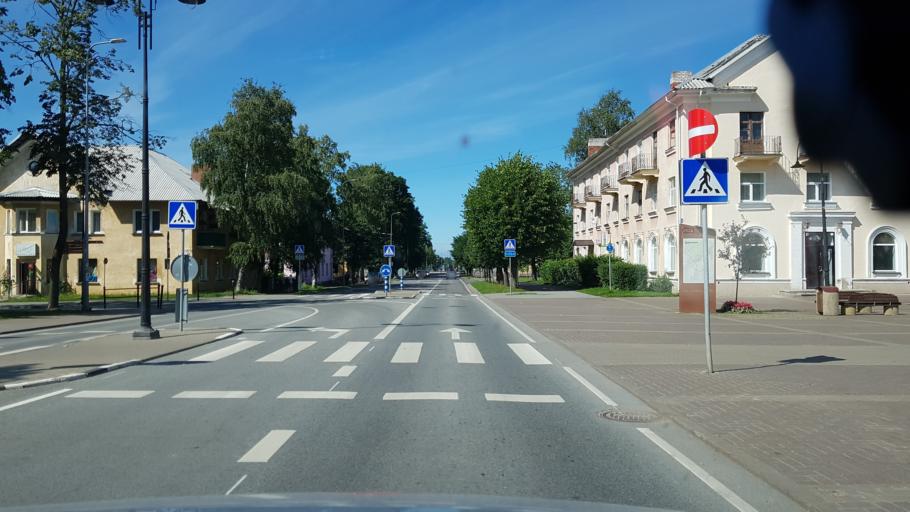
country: EE
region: Ida-Virumaa
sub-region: Kohtla-Jaerve linn
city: Kohtla-Jarve
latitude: 59.4022
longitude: 27.2874
